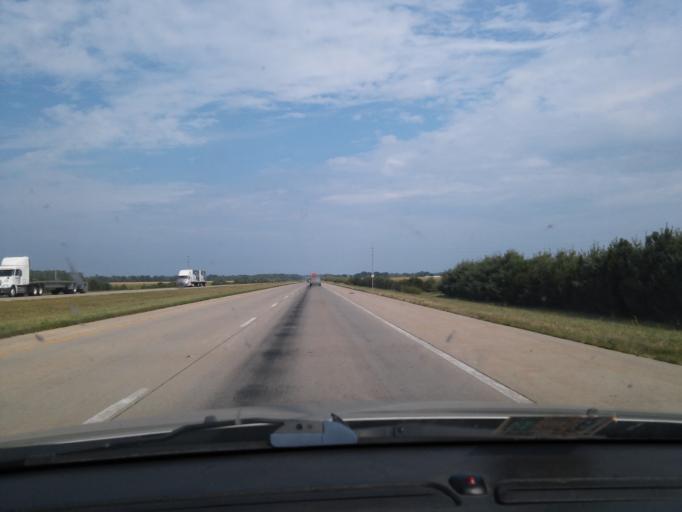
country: US
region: Ohio
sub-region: Greene County
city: Wilberforce
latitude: 39.6830
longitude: -83.8384
